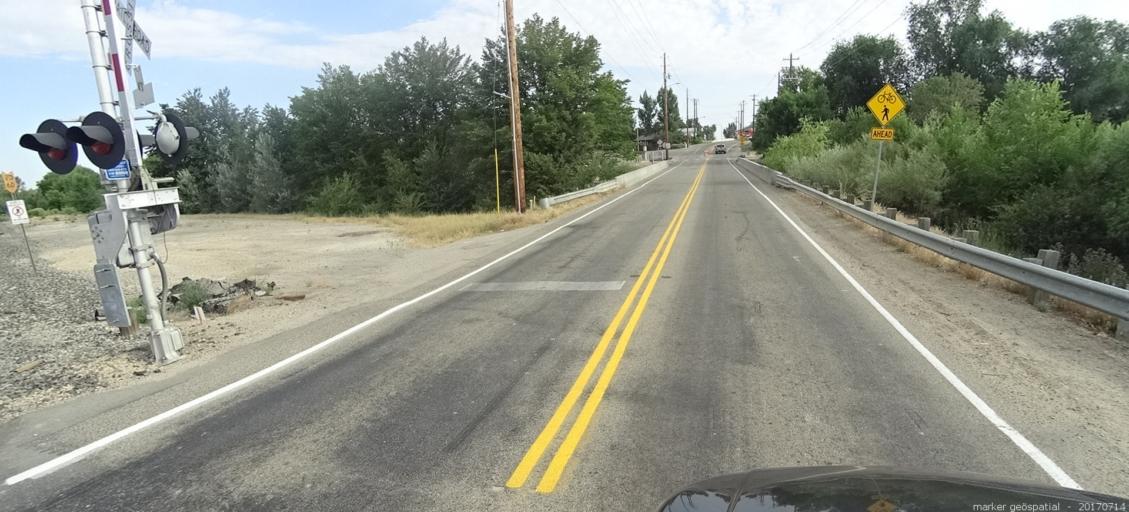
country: US
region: Idaho
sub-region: Ada County
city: Kuna
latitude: 43.4870
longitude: -116.4138
